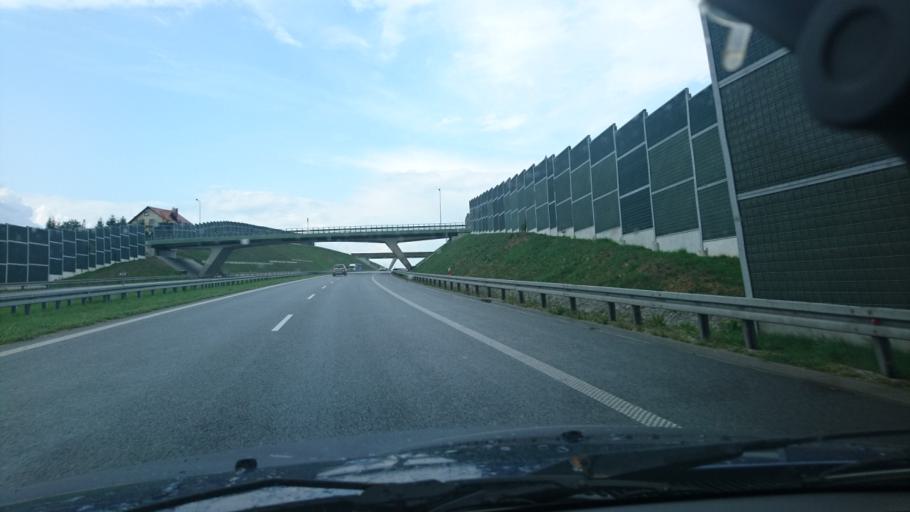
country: PL
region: Silesian Voivodeship
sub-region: Powiat zywiecki
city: Lesna
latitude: 49.6898
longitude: 19.1378
